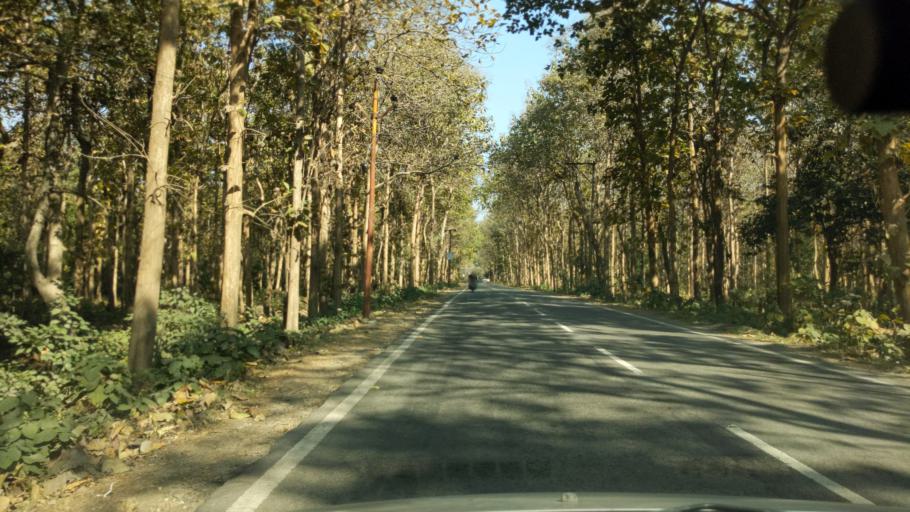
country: IN
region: Uttarakhand
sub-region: Naini Tal
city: Ramnagar
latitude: 29.3812
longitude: 79.1428
